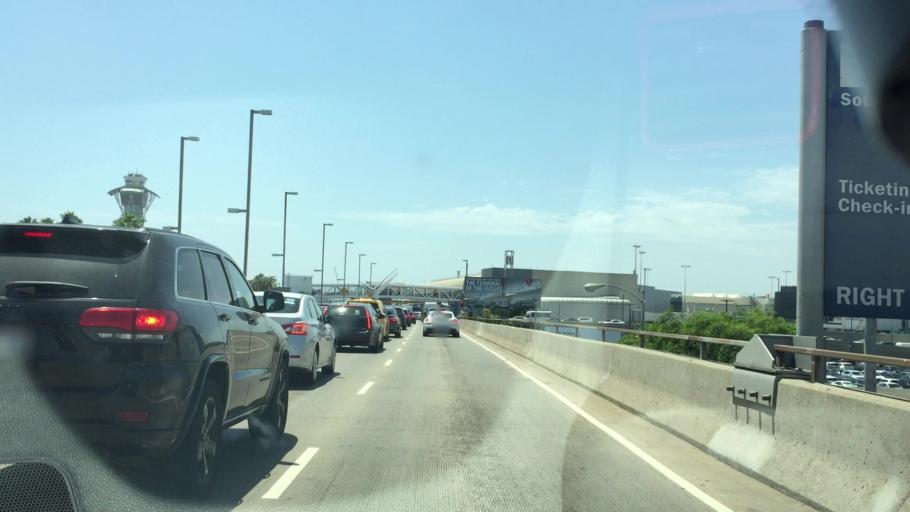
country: US
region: California
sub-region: Los Angeles County
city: El Segundo
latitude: 33.9454
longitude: -118.3975
